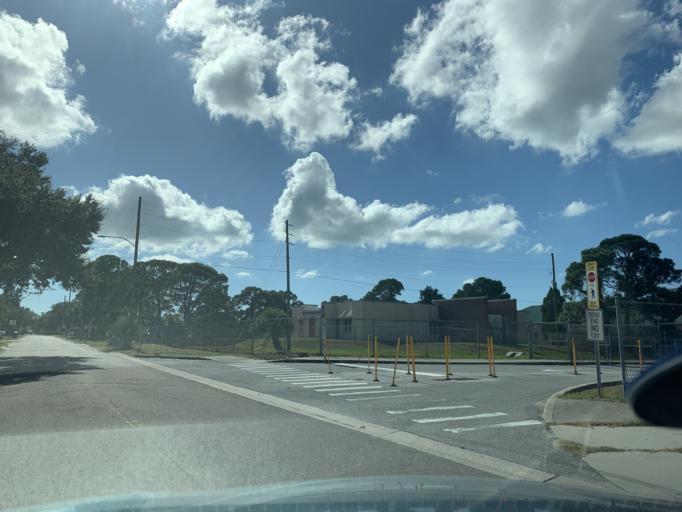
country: US
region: Florida
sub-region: Pinellas County
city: Kenneth City
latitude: 27.8081
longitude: -82.7383
